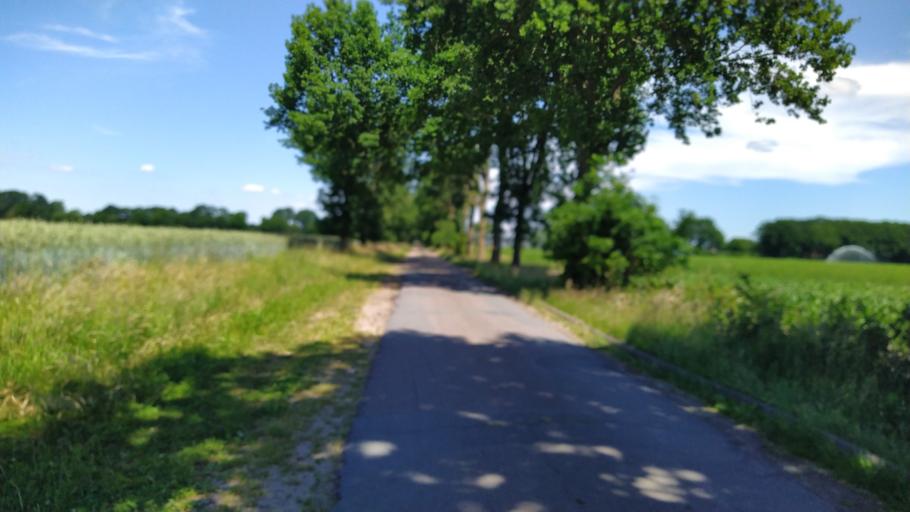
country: DE
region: Lower Saxony
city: Deinste
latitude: 53.5128
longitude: 9.4398
